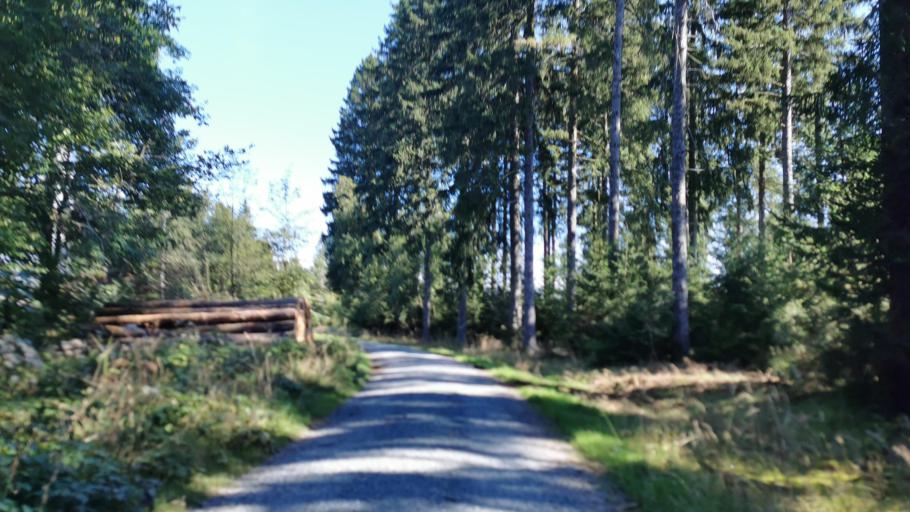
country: DE
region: Bavaria
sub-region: Upper Franconia
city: Ludwigsstadt
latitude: 50.4483
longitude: 11.3564
